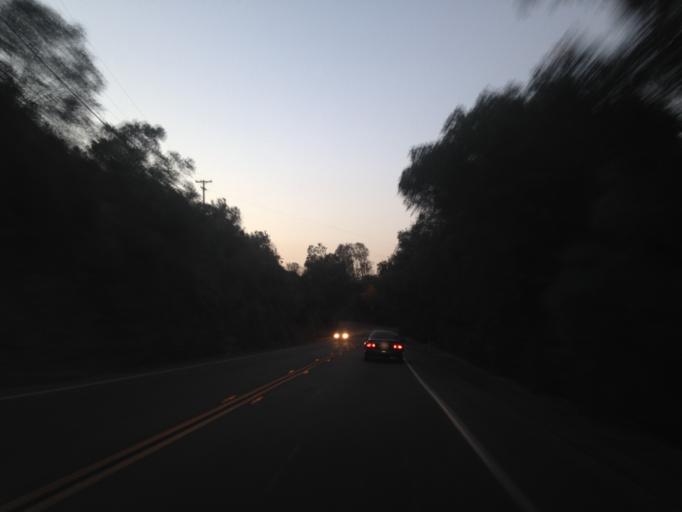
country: US
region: California
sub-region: San Diego County
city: Bonsall
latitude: 33.2549
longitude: -117.2079
